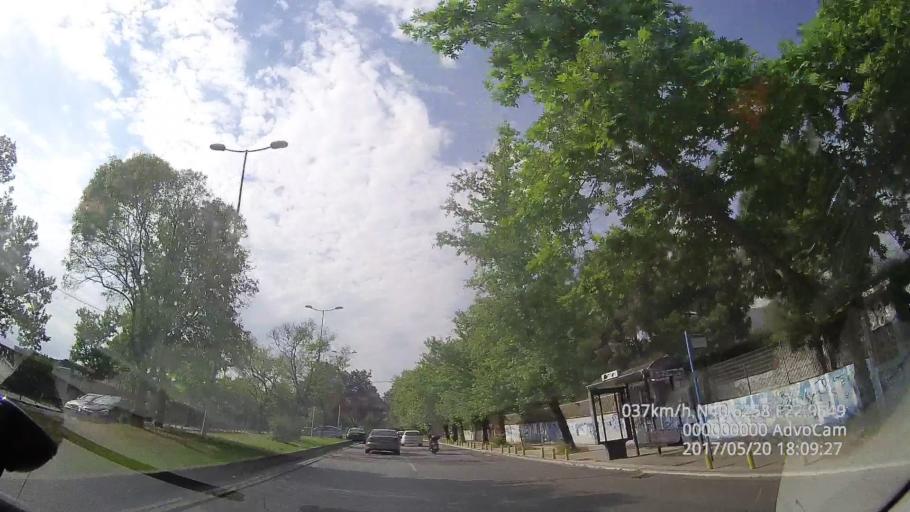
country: GR
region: Central Macedonia
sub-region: Nomos Thessalonikis
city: Agios Pavlos
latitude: 40.6261
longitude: 22.9647
